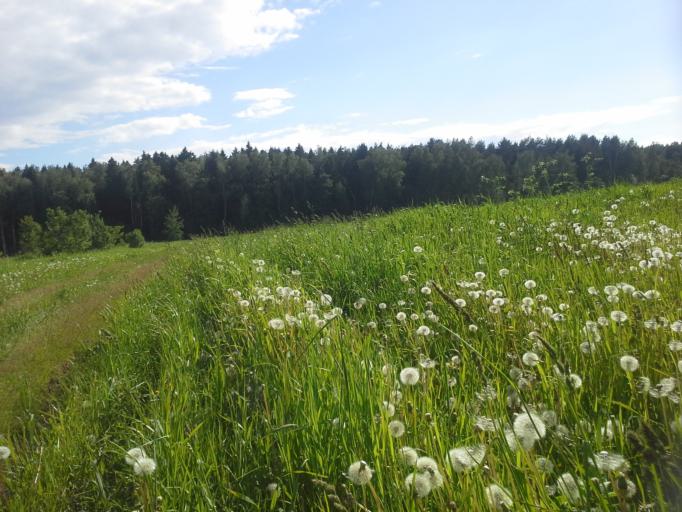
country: RU
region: Moskovskaya
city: Filimonki
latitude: 55.5577
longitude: 37.3940
